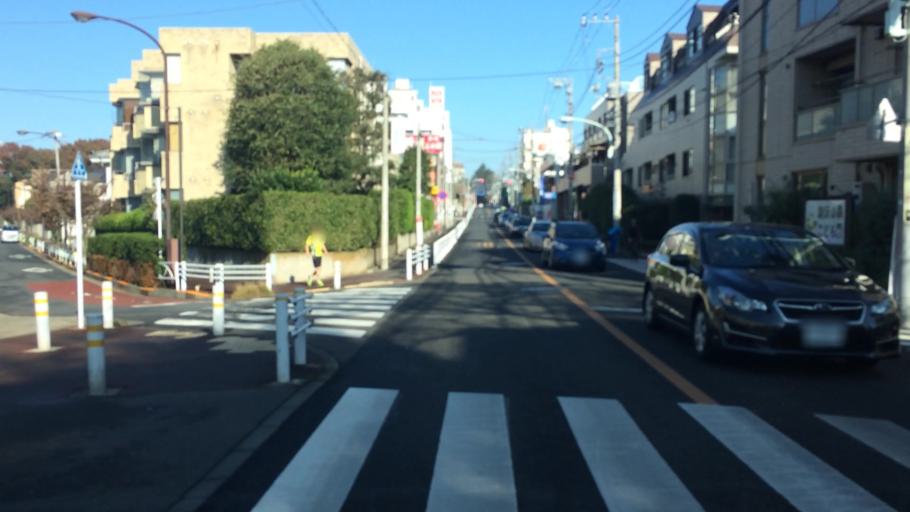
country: JP
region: Tokyo
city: Tokyo
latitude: 35.6211
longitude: 139.6669
